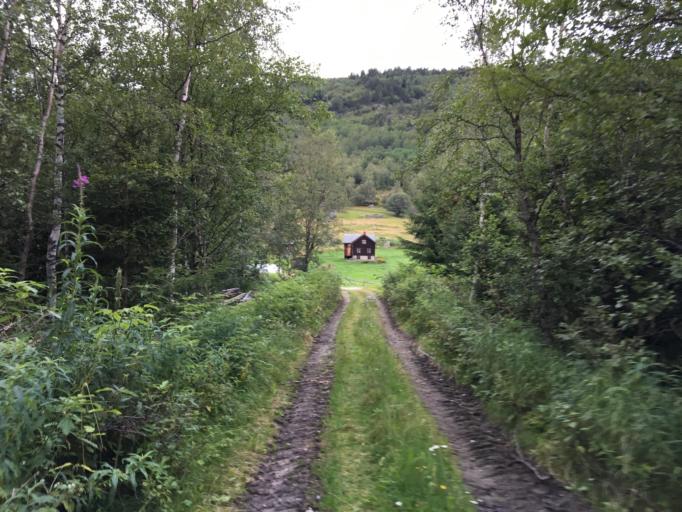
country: NO
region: Buskerud
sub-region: Hol
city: Hol
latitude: 60.6183
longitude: 8.2236
